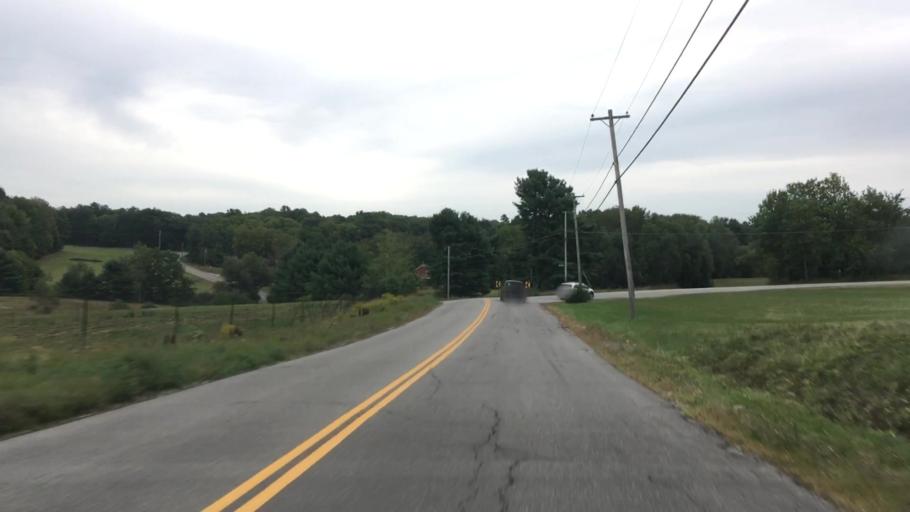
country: US
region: Maine
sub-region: Cumberland County
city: Freeport
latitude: 43.8904
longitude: -70.1805
